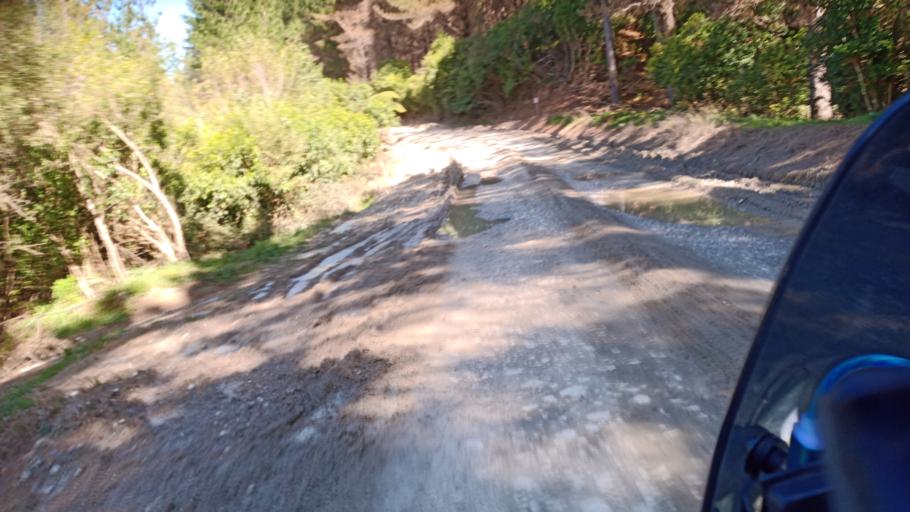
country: NZ
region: Gisborne
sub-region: Gisborne District
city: Gisborne
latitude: -38.9030
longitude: 177.8039
